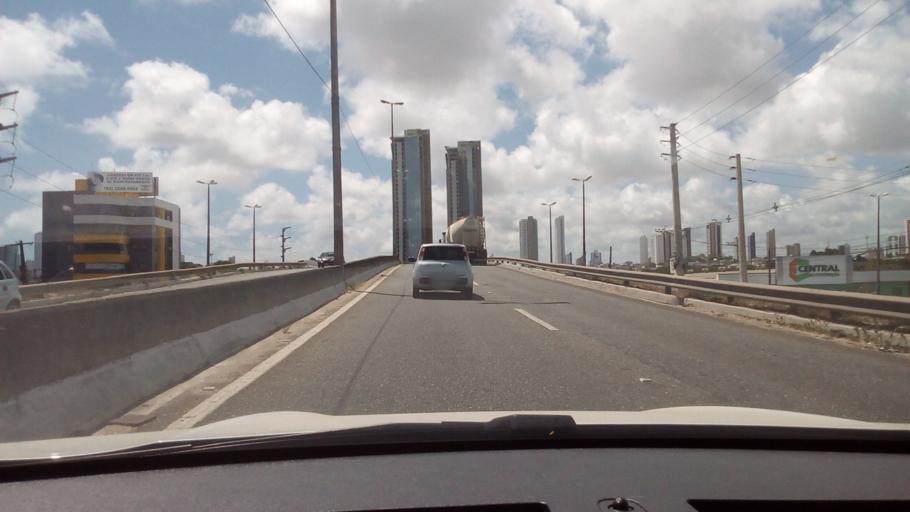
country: BR
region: Paraiba
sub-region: Joao Pessoa
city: Joao Pessoa
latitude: -7.0972
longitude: -34.8480
